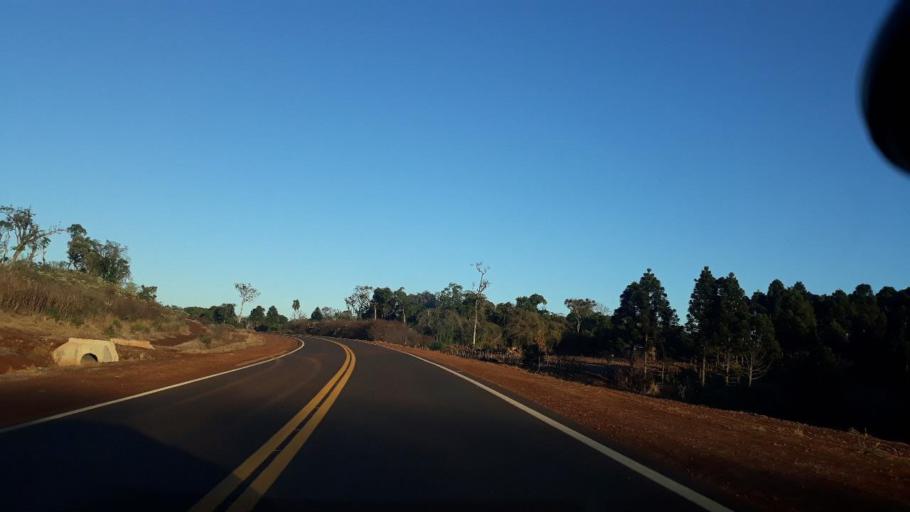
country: AR
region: Misiones
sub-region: Departamento de San Pedro
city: San Pedro
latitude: -26.5362
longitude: -53.9540
